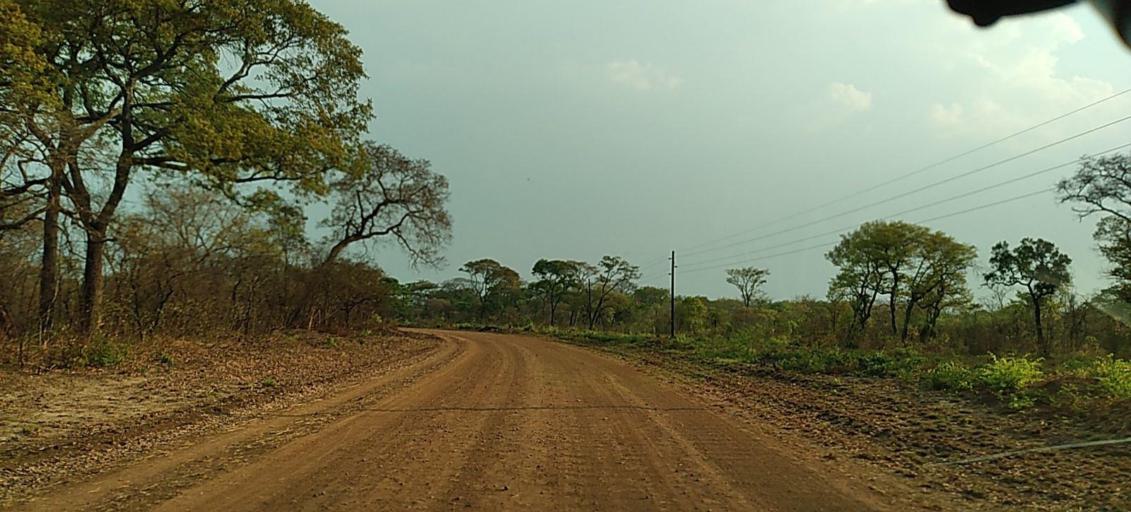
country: ZM
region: Western
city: Lukulu
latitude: -13.9943
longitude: 23.6154
